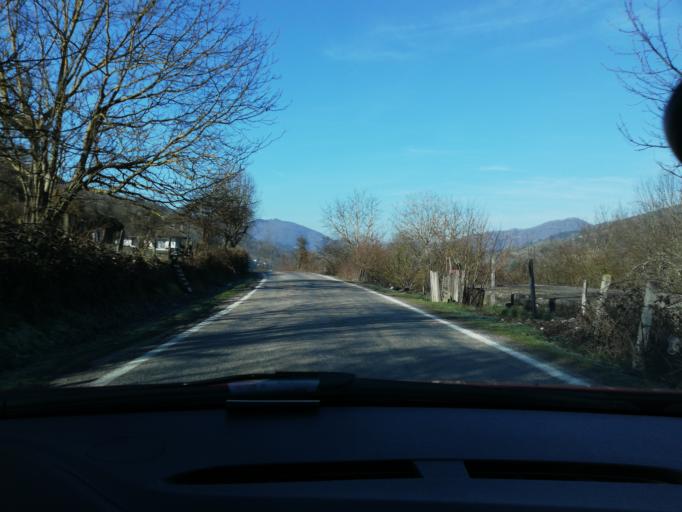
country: TR
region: Bartin
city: Kumluca
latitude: 41.4538
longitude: 32.4998
